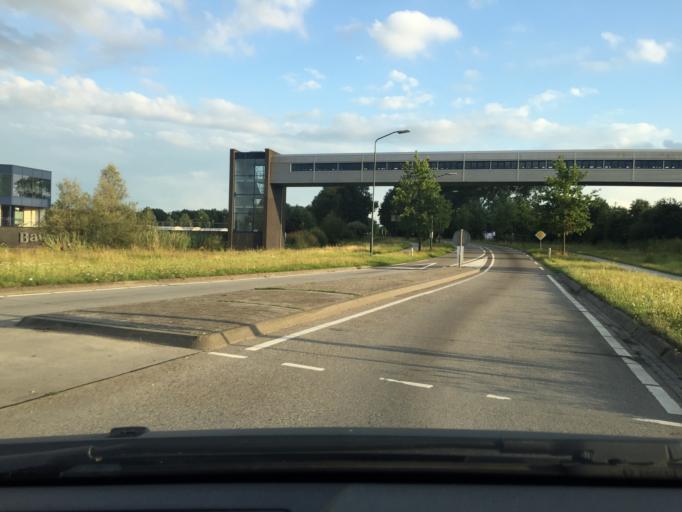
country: NL
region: North Brabant
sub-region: Gemeente Laarbeek
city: Aarle-Rixtel
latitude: 51.5179
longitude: 5.6064
